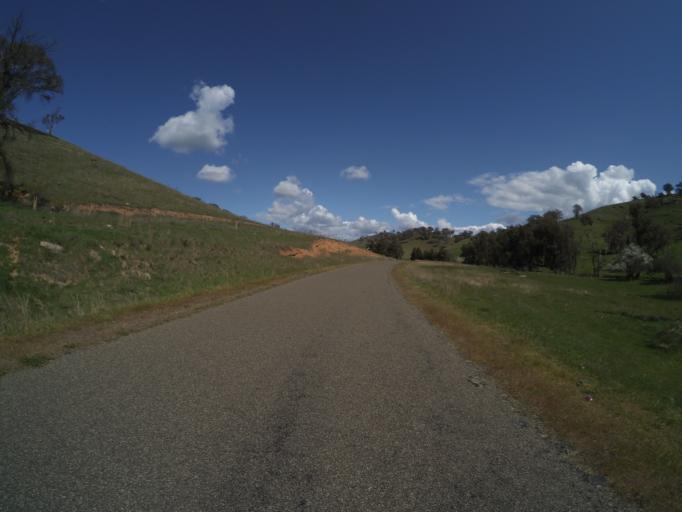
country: AU
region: New South Wales
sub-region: Yass Valley
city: Murrumbateman
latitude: -35.0520
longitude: 148.8404
